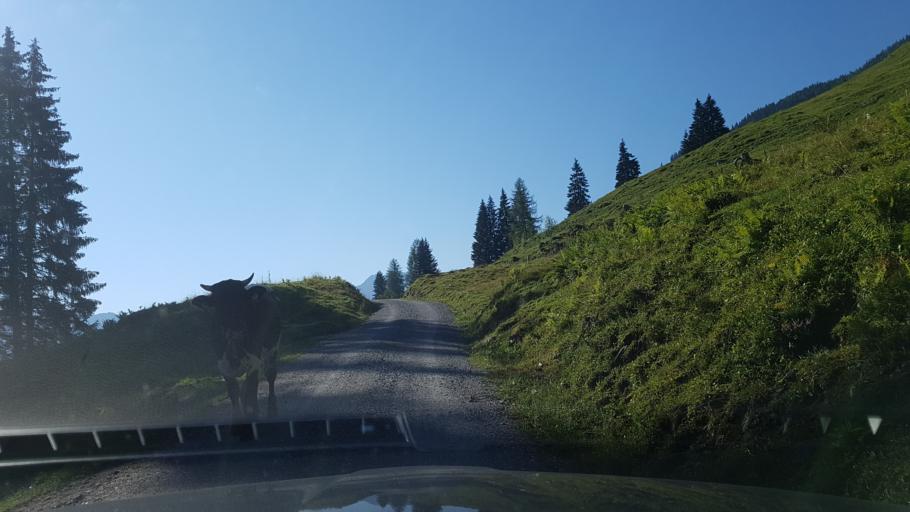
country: AT
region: Salzburg
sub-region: Politischer Bezirk Sankt Johann im Pongau
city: Dorfgastein
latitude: 47.2481
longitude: 13.0742
